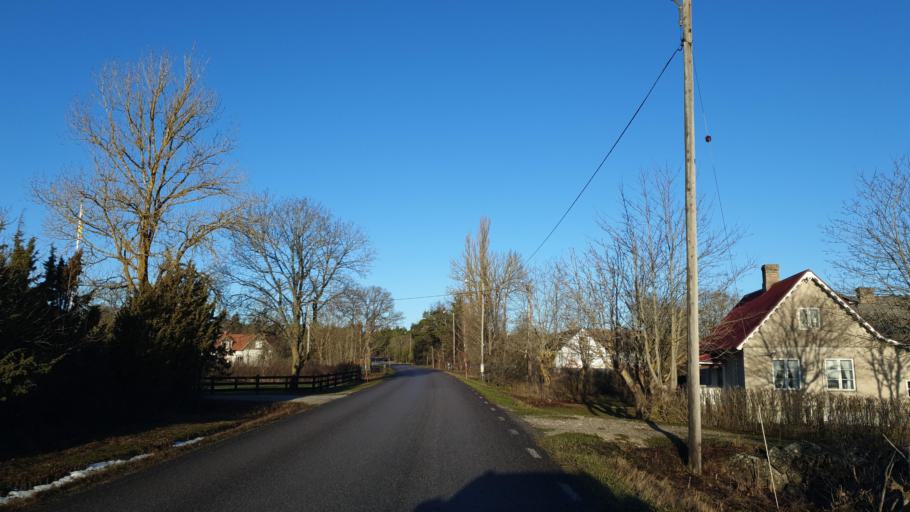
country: SE
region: Gotland
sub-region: Gotland
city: Slite
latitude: 57.7088
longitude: 18.7573
